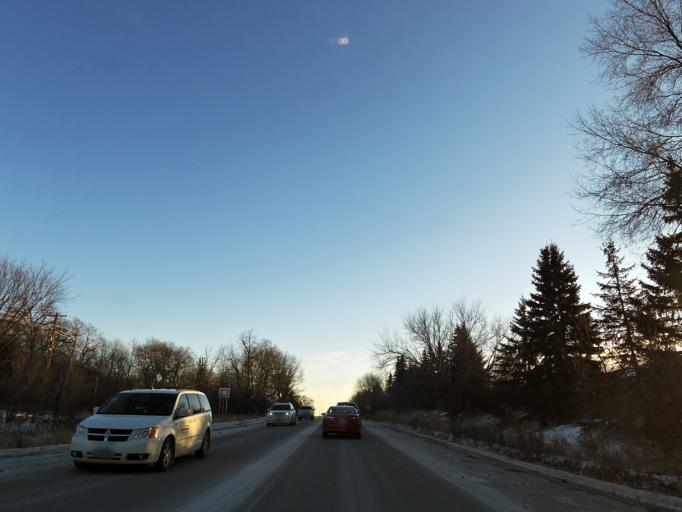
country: US
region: Minnesota
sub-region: Carver County
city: Chaska
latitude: 44.8238
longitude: -93.6027
